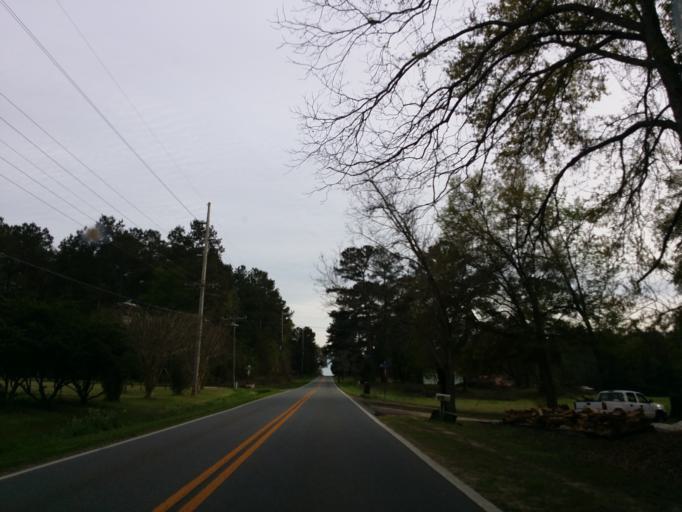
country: US
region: Florida
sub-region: Leon County
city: Tallahassee
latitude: 30.4966
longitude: -84.1255
